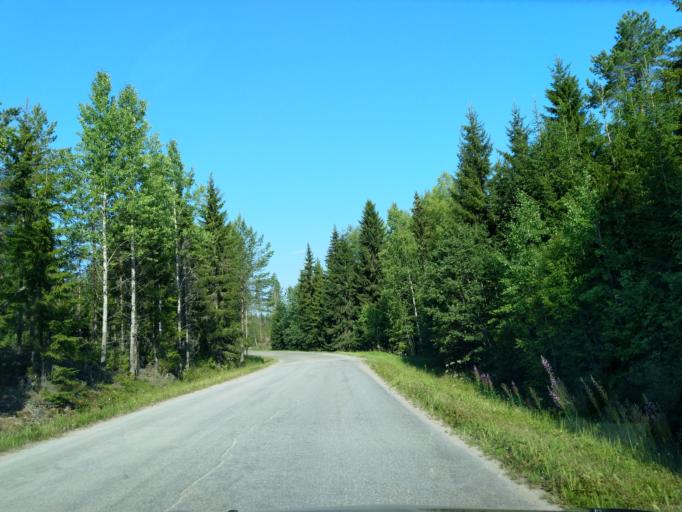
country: FI
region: Satakunta
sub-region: Pori
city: Laengelmaeki
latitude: 61.7262
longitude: 22.2020
